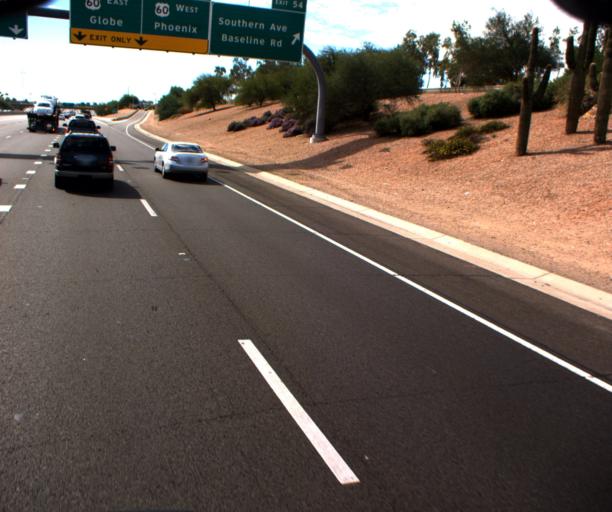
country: US
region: Arizona
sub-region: Maricopa County
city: Tempe
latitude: 33.3990
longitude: -111.8914
